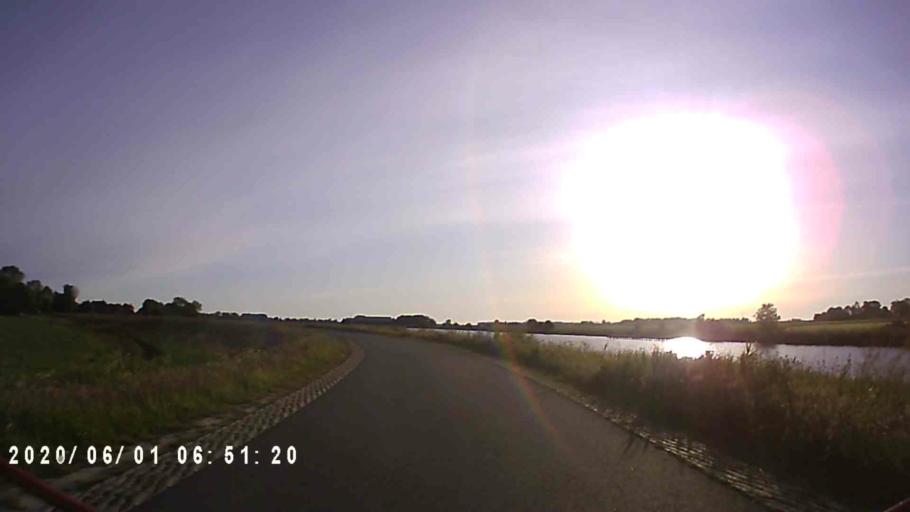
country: NL
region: Friesland
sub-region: Gemeente Kollumerland en Nieuwkruisland
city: Kollum
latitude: 53.3048
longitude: 6.1314
